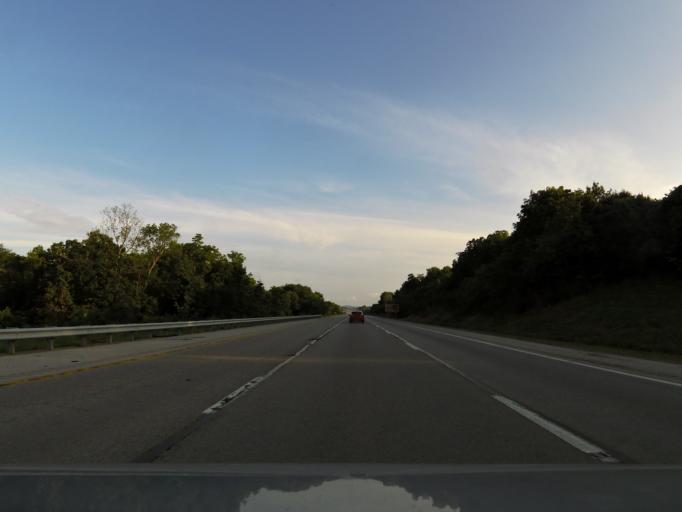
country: US
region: Kentucky
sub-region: Madison County
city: Richmond
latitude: 37.6592
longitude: -84.3124
